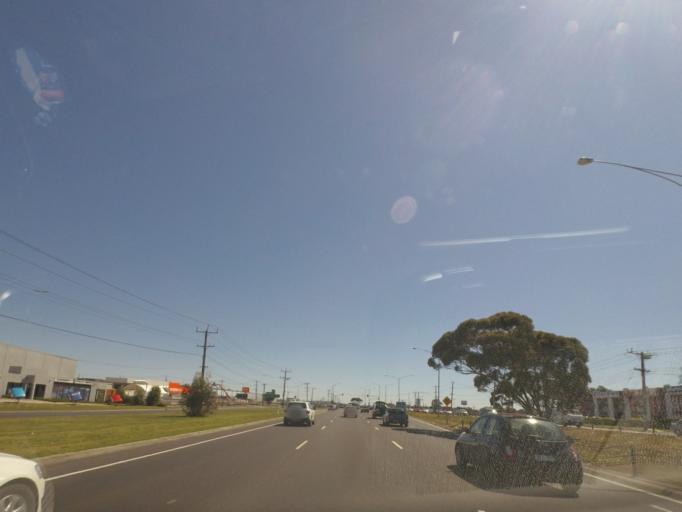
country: AU
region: Victoria
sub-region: Hume
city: Coolaroo
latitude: -37.6453
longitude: 144.9514
